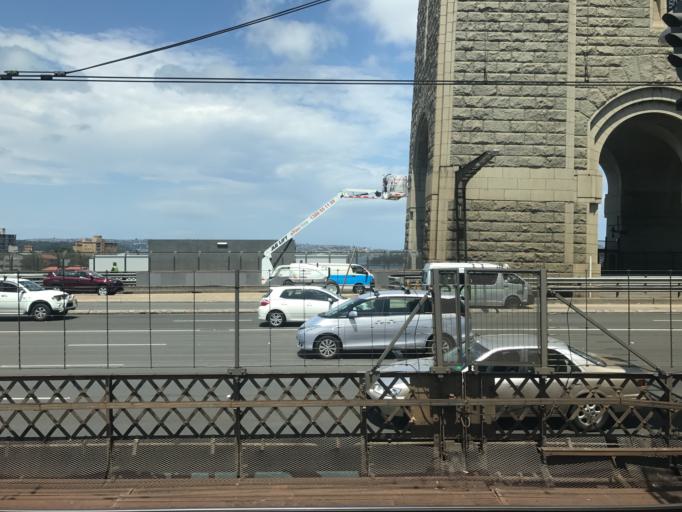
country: AU
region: New South Wales
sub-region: North Sydney
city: Milsons Point
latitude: -33.8500
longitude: 151.2120
